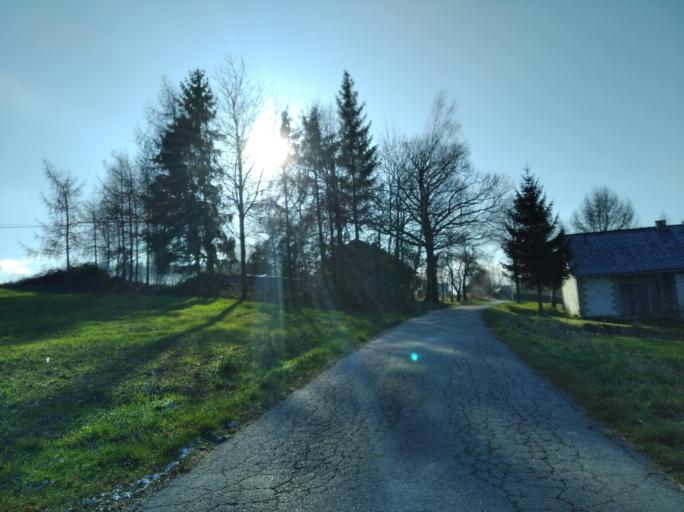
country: PL
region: Subcarpathian Voivodeship
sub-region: Powiat strzyzowski
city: Polomia
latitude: 49.8863
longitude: 21.8500
